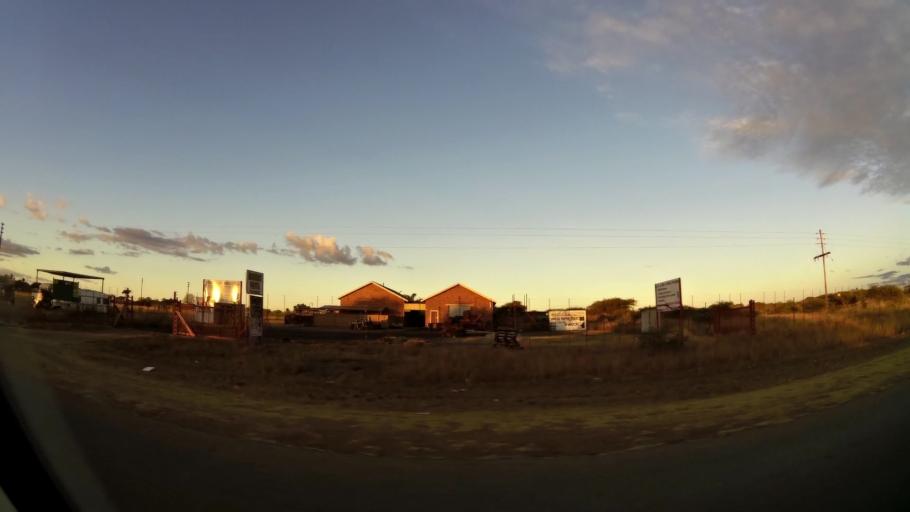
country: ZA
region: Limpopo
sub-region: Capricorn District Municipality
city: Polokwane
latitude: -23.8076
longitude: 29.4794
